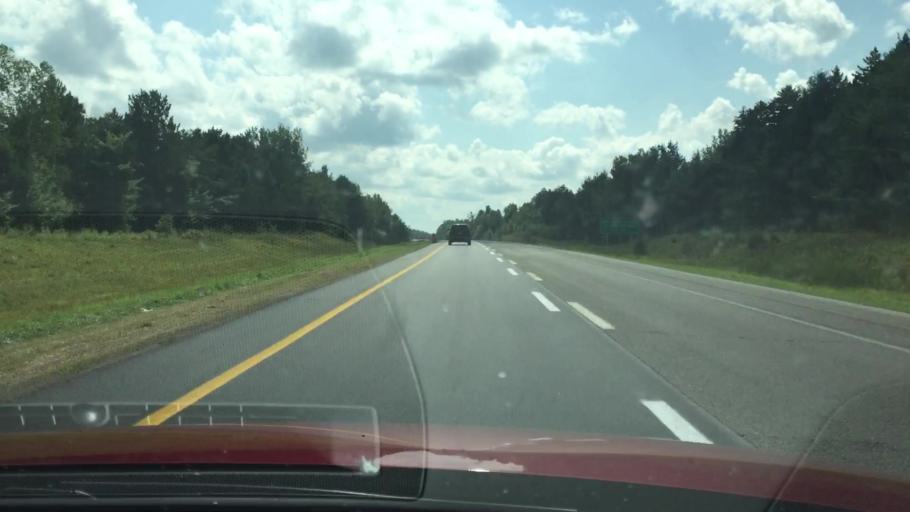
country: US
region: Maine
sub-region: Penobscot County
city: Medway
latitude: 45.6300
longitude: -68.5054
